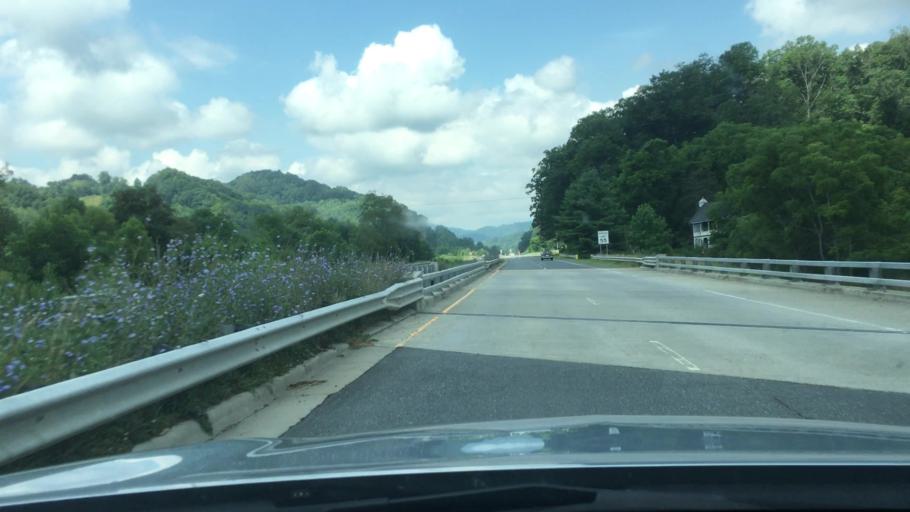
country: US
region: North Carolina
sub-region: Yancey County
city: Burnsville
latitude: 35.9134
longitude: -82.4007
